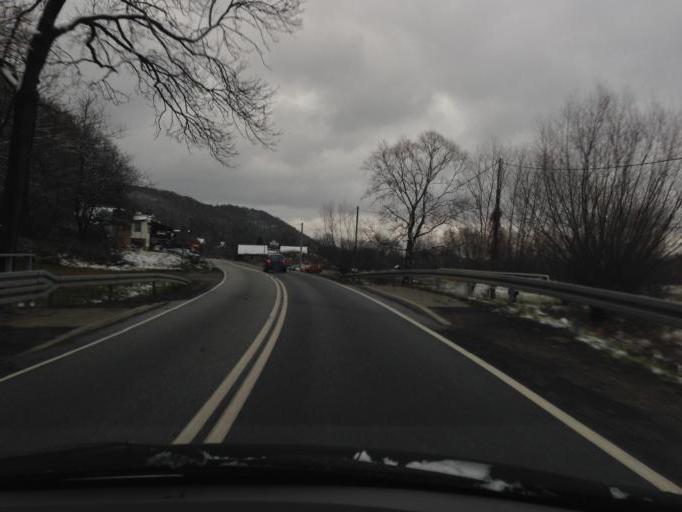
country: PL
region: Lesser Poland Voivodeship
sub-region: Powiat tarnowski
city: Zakliczyn
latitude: 49.8673
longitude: 20.7736
